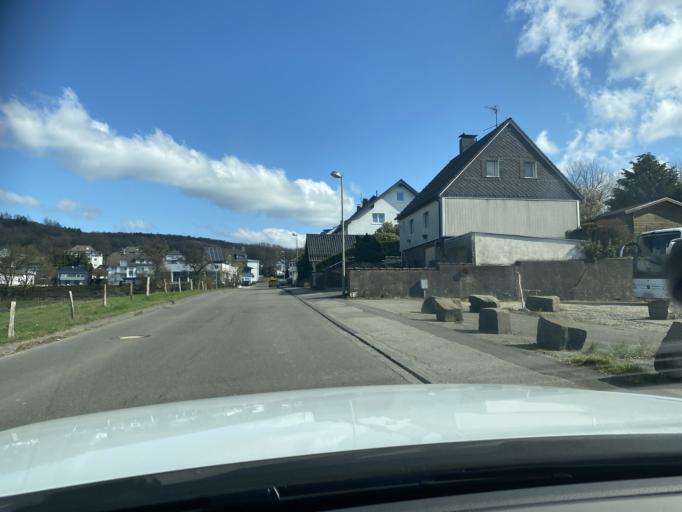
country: DE
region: North Rhine-Westphalia
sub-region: Regierungsbezirk Koln
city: Lindlar
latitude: 51.0215
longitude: 7.3673
